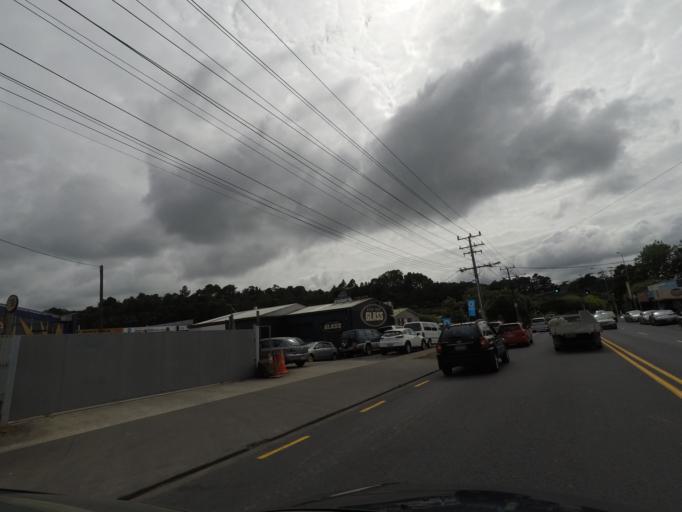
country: NZ
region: Auckland
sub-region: Auckland
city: Waitakere
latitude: -36.9087
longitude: 174.6405
